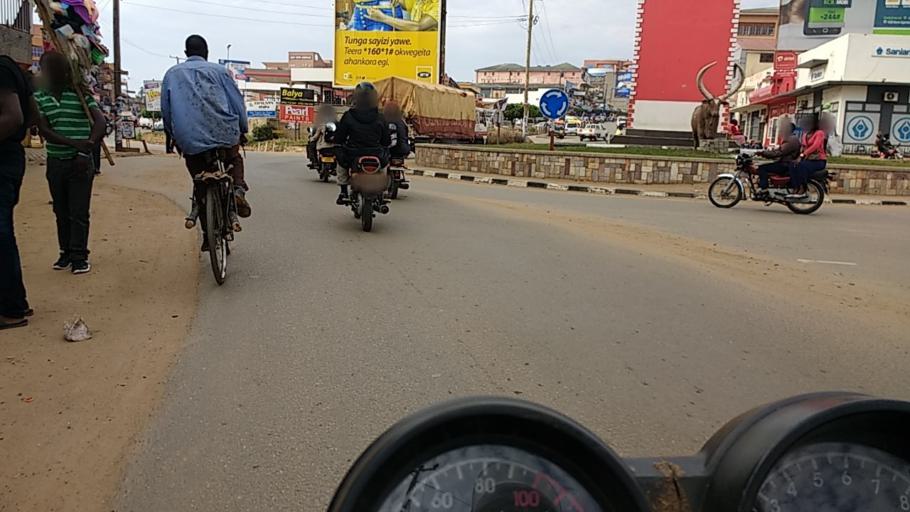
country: UG
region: Western Region
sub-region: Mbarara District
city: Mbarara
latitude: -0.6026
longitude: 30.6632
